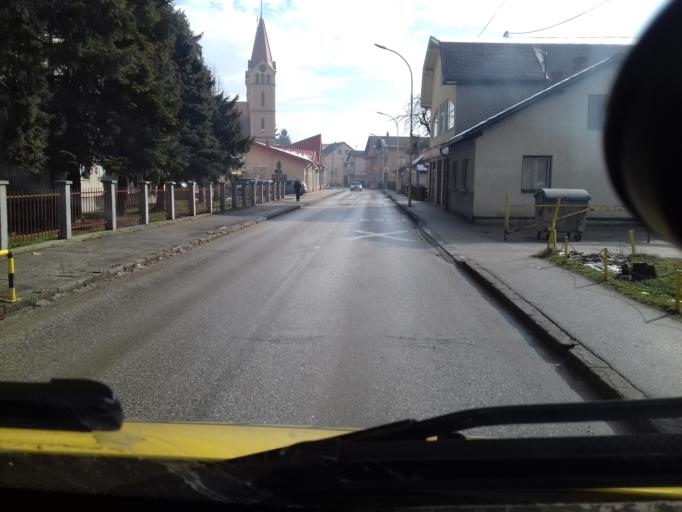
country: BA
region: Federation of Bosnia and Herzegovina
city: Zepce
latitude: 44.4240
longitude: 18.0381
